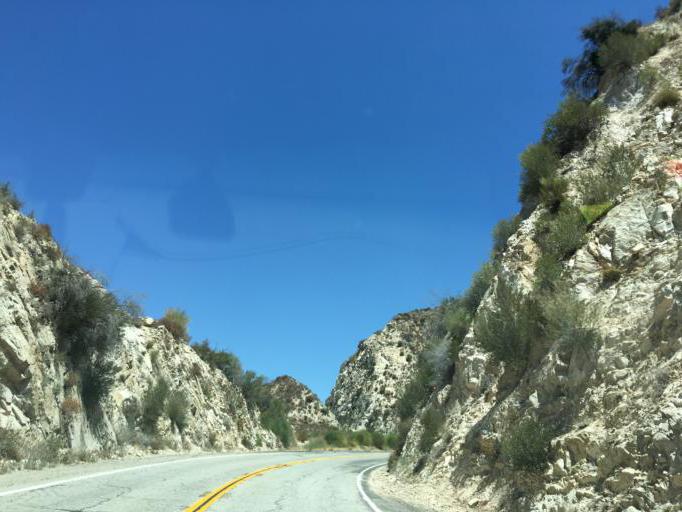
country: US
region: California
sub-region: Los Angeles County
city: La Crescenta-Montrose
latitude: 34.2954
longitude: -118.1722
